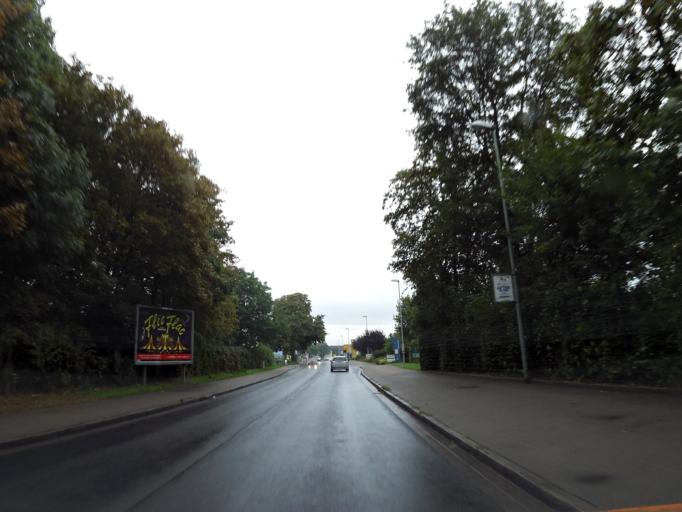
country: DE
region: Lower Saxony
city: Goettingen
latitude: 51.5527
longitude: 9.9203
